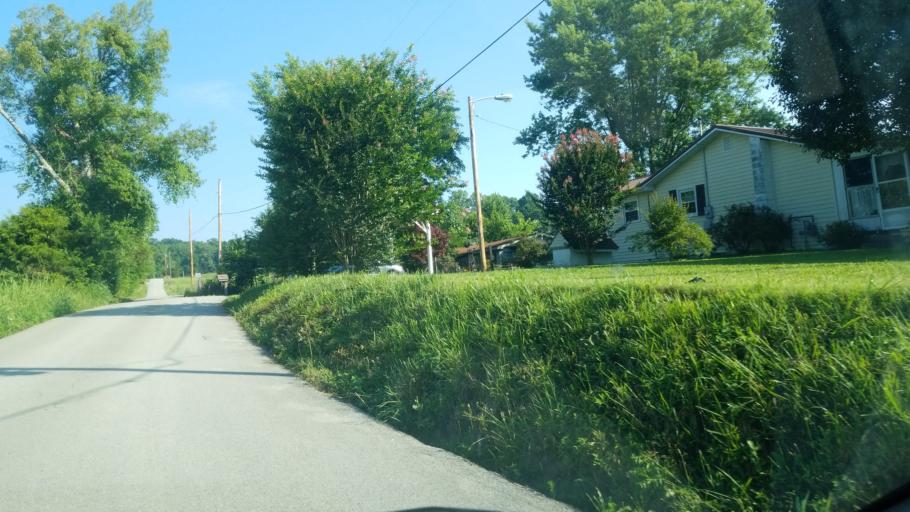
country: US
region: Tennessee
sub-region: Loudon County
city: Loudon
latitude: 35.8128
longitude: -84.3425
